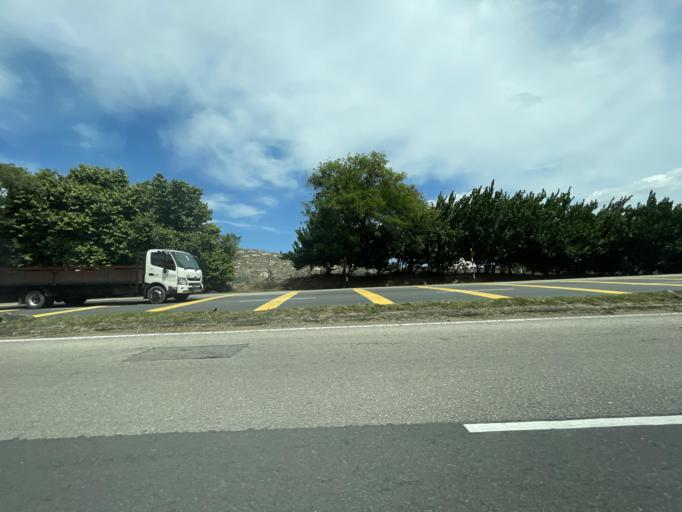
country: MY
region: Melaka
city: Batu Berendam
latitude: 2.2393
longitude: 102.2245
